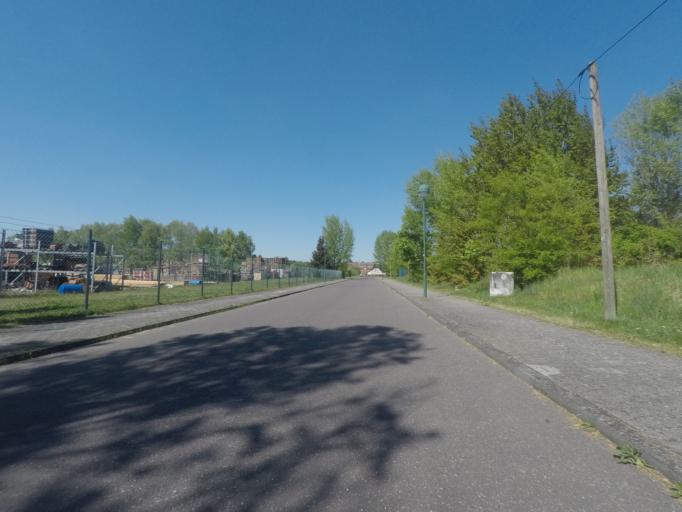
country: DE
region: Brandenburg
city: Melchow
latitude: 52.8497
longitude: 13.6971
